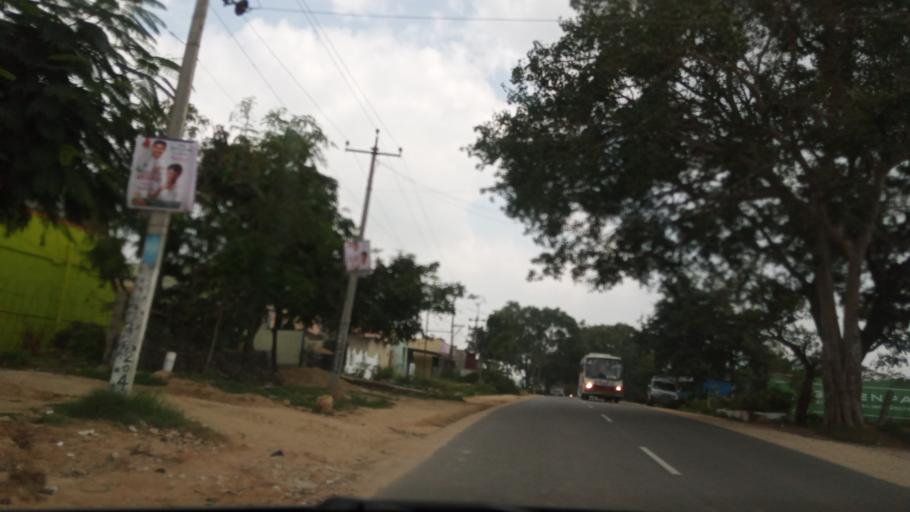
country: IN
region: Andhra Pradesh
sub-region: Chittoor
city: Madanapalle
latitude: 13.6429
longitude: 78.5693
